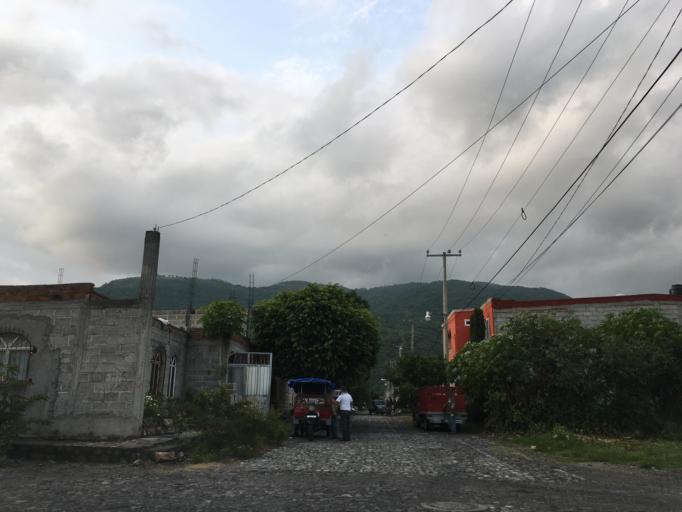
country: MX
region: Nayarit
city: Jala
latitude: 21.0998
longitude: -104.4361
